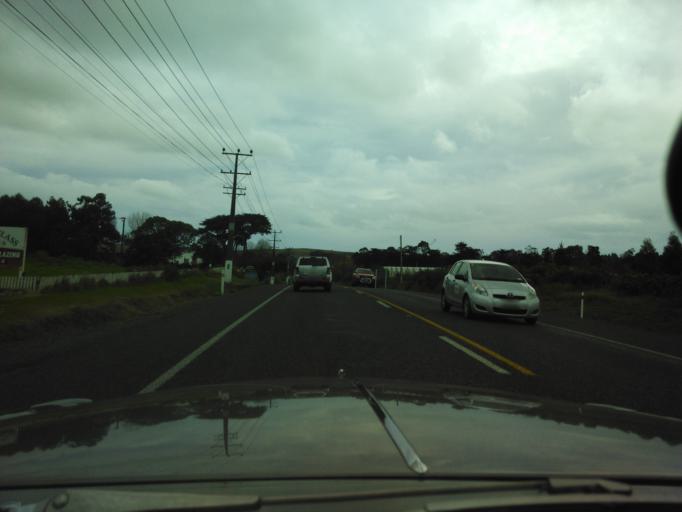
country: NZ
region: Auckland
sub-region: Auckland
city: Muriwai Beach
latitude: -36.7664
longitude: 174.5090
